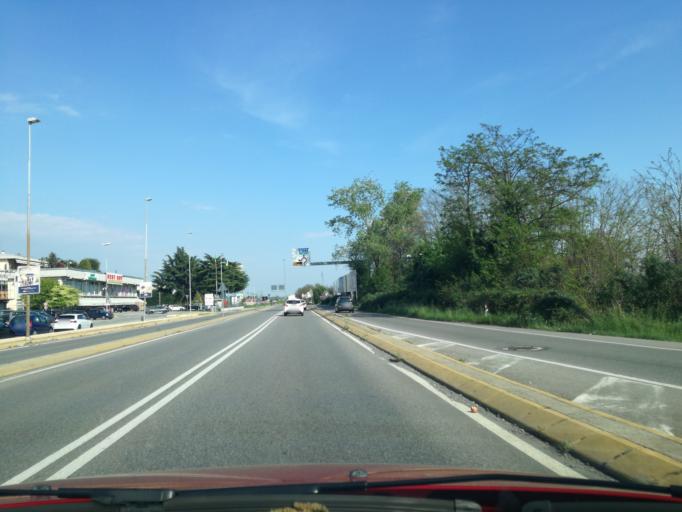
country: IT
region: Lombardy
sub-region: Provincia di Monza e Brianza
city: Cornate d'Adda
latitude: 45.6195
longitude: 9.4749
